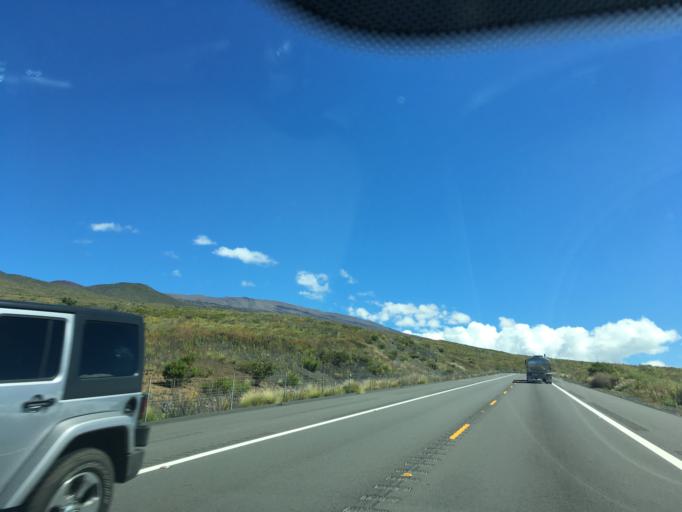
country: US
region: Hawaii
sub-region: Hawaii County
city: Waikoloa
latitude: 19.7790
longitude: -155.6009
